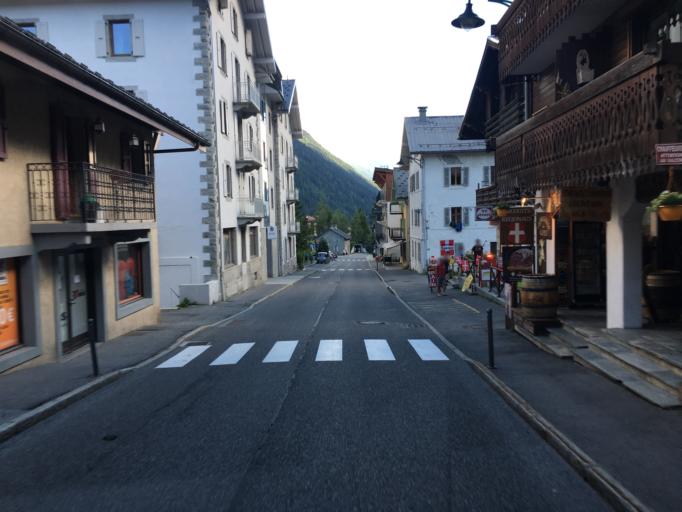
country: FR
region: Rhone-Alpes
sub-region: Departement de la Haute-Savoie
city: Chamonix-Mont-Blanc
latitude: 45.9835
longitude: 6.9265
